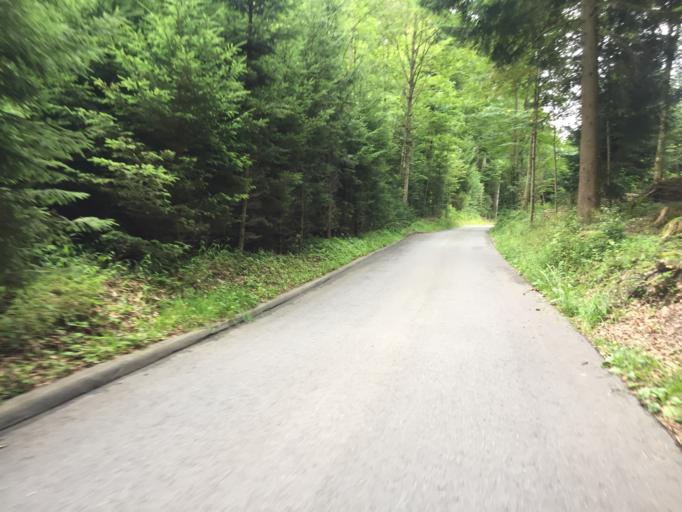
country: CH
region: Bern
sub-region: Bern-Mittelland District
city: Stettlen
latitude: 46.9474
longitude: 7.5221
